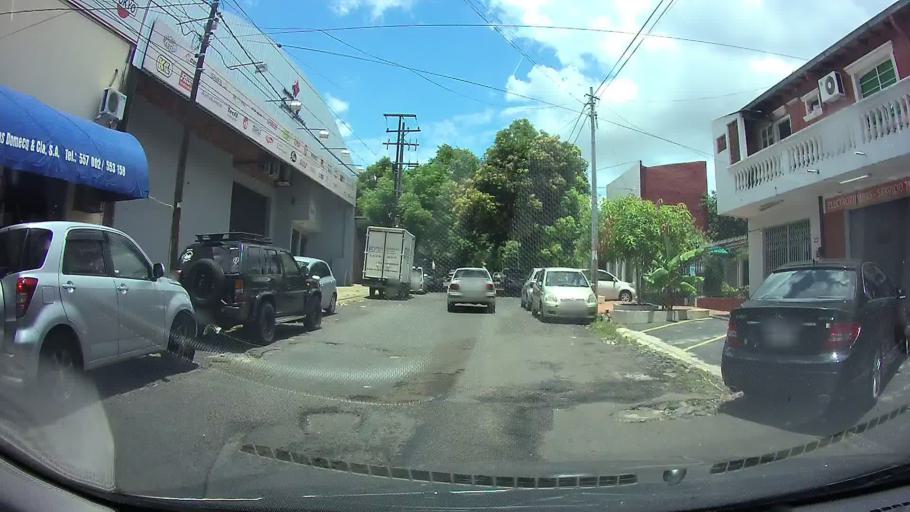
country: PY
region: Central
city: Lambare
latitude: -25.3109
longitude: -57.5928
